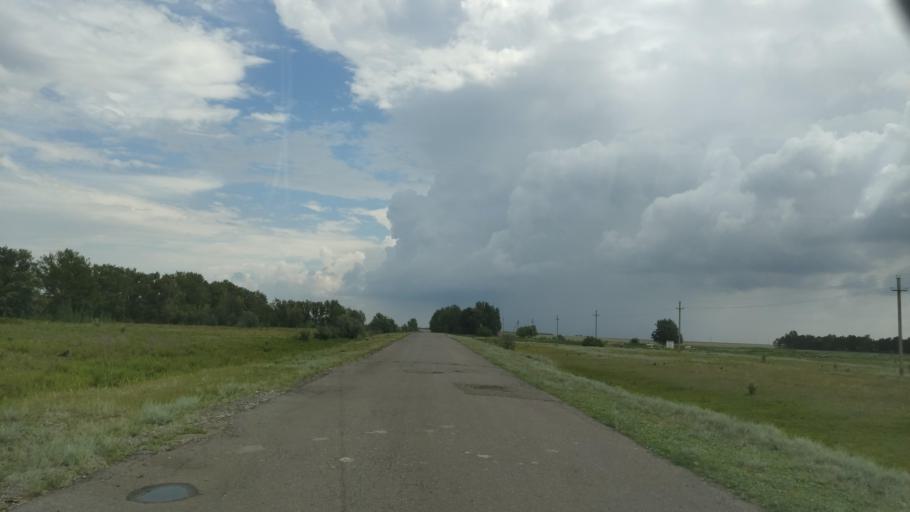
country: KZ
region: Pavlodar
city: Pavlodar
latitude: 52.6357
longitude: 77.3253
